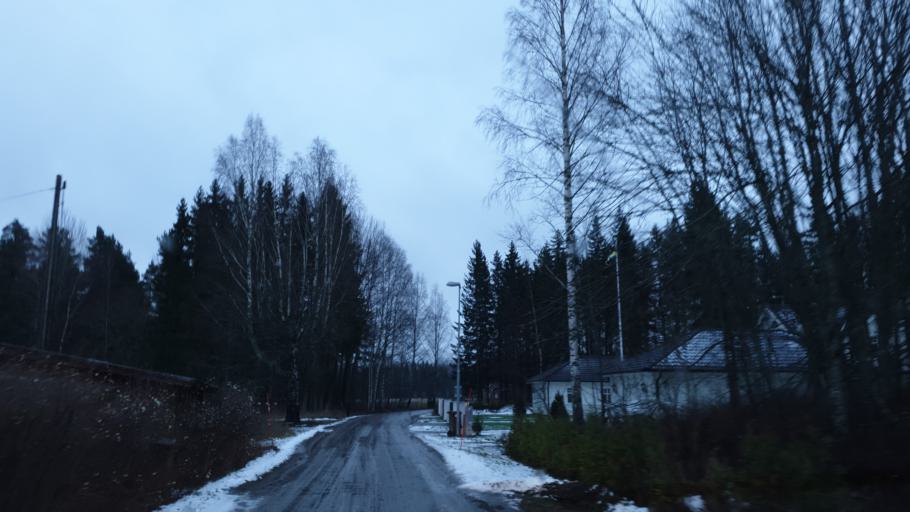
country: SE
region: Uppsala
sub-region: Tierps Kommun
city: Tierp
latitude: 60.3418
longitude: 17.4735
